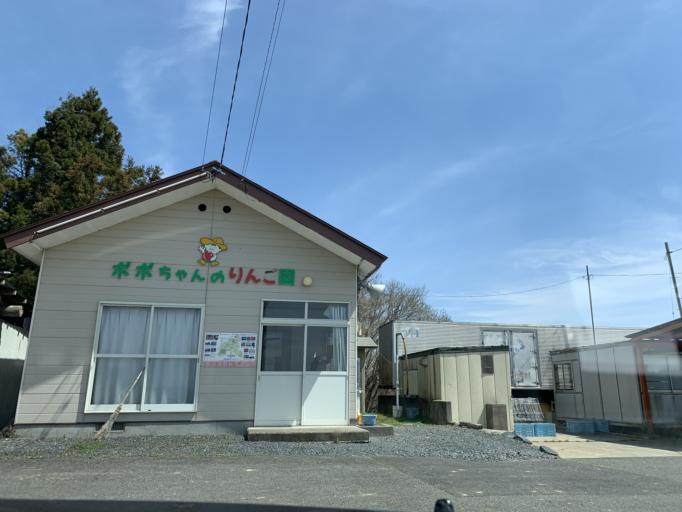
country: JP
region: Iwate
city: Ichinoseki
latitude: 38.8412
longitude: 141.2890
